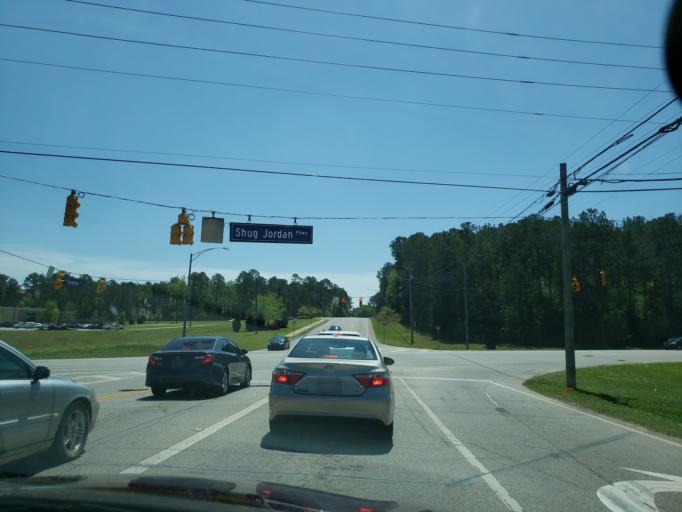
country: US
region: Alabama
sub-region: Lee County
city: Auburn
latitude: 32.6311
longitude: -85.4978
